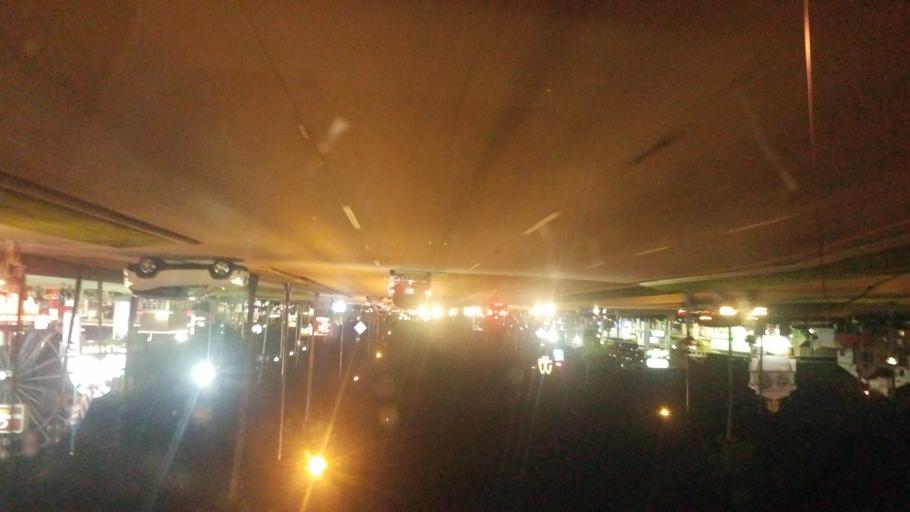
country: US
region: Florida
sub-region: Osceola County
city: Celebration
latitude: 28.3327
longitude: -81.5169
